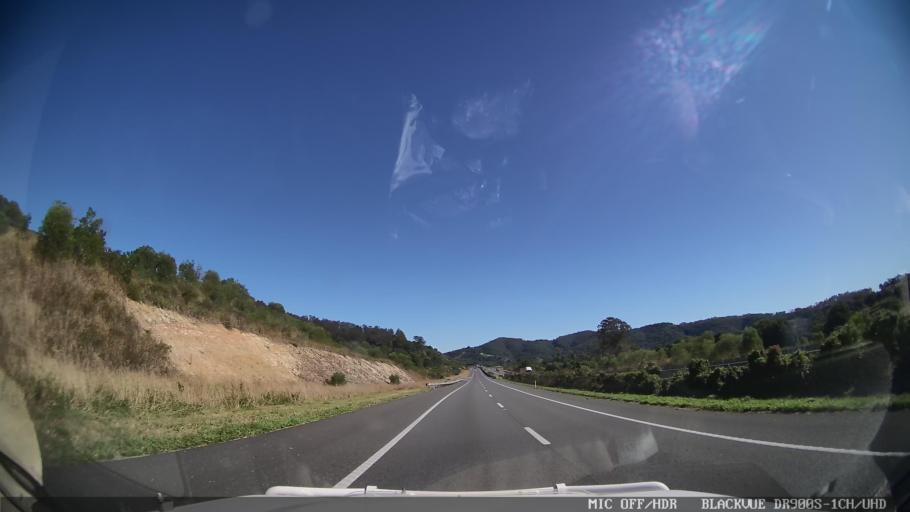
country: AU
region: Queensland
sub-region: Sunshine Coast
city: Black Mountain
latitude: -26.3934
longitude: 152.8159
